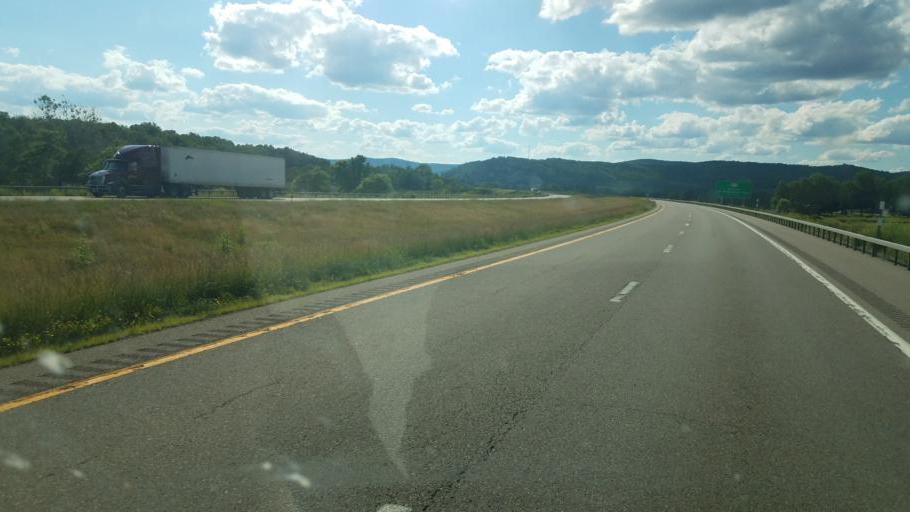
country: US
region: New York
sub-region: Cattaraugus County
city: Allegany
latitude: 42.1000
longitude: -78.4811
